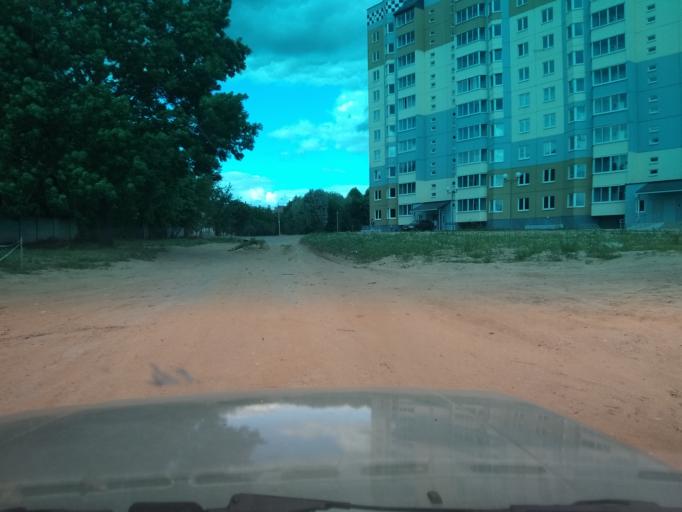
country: BY
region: Mogilev
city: Mahilyow
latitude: 53.9229
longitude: 30.3536
